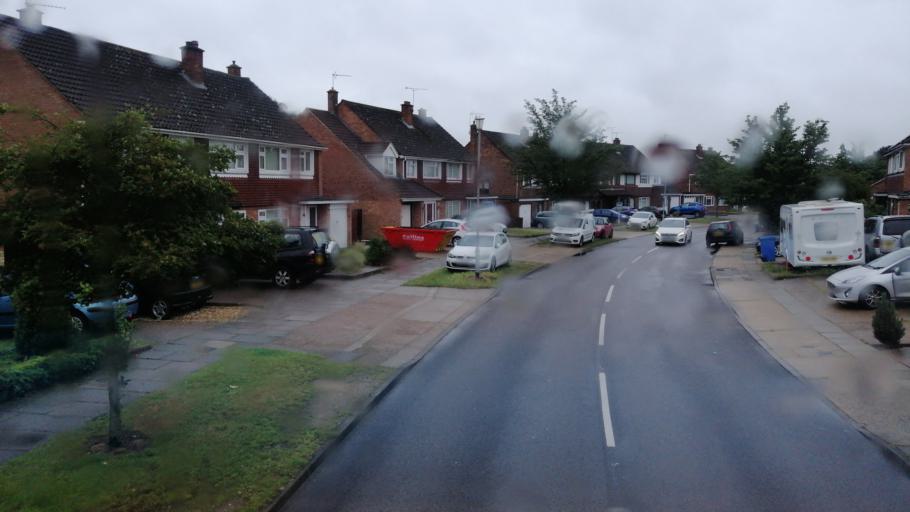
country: GB
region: England
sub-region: Suffolk
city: Kesgrave
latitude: 52.0437
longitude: 1.2034
